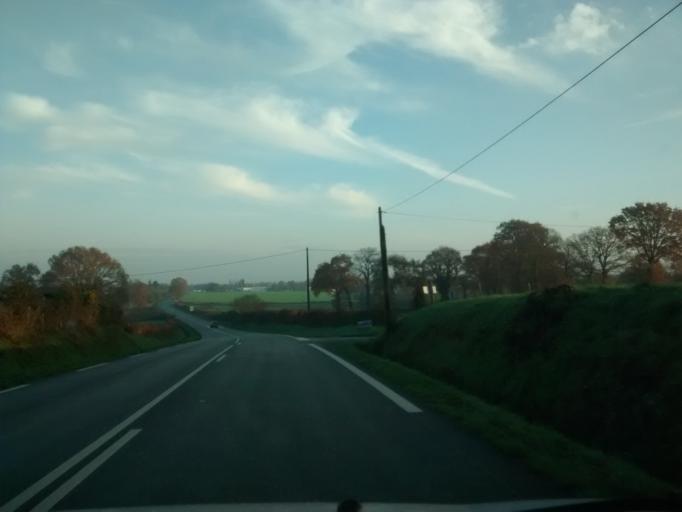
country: FR
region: Brittany
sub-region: Departement d'Ille-et-Vilaine
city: Sens-de-Bretagne
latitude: 48.3225
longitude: -1.5301
